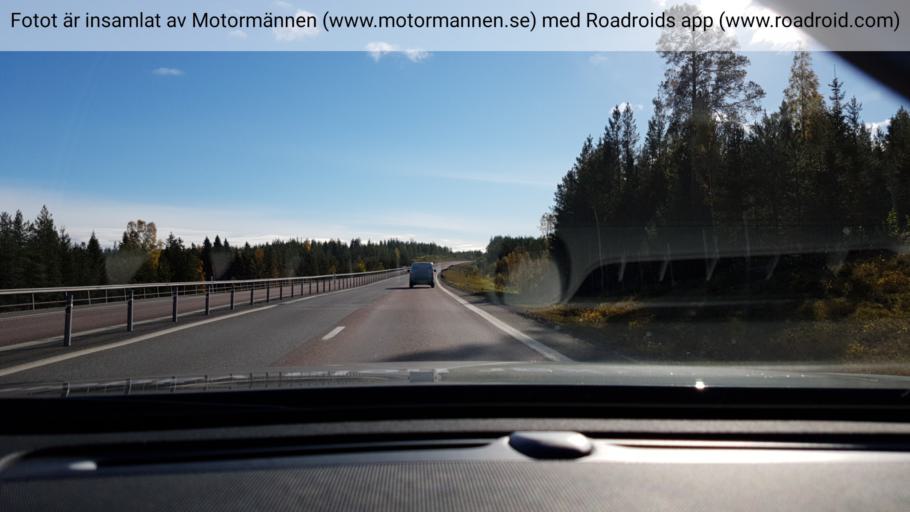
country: SE
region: Vaesterbotten
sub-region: Skelleftea Kommun
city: Soedra Bergsbyn
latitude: 64.6856
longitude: 21.0595
